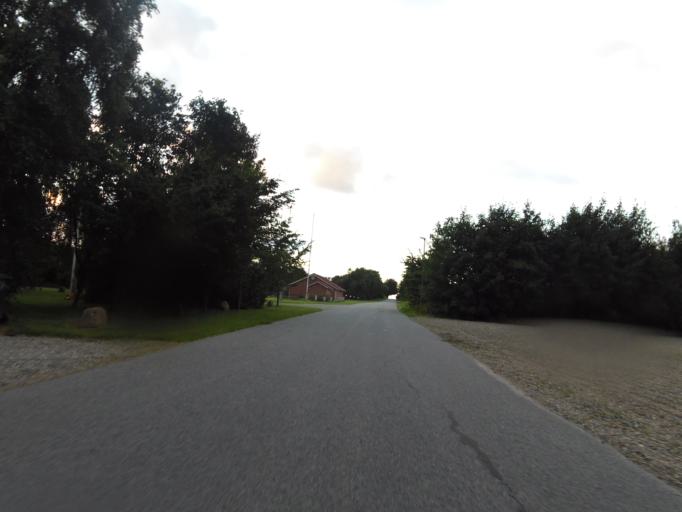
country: DK
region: South Denmark
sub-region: Esbjerg Kommune
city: Ribe
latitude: 55.2823
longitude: 8.8316
